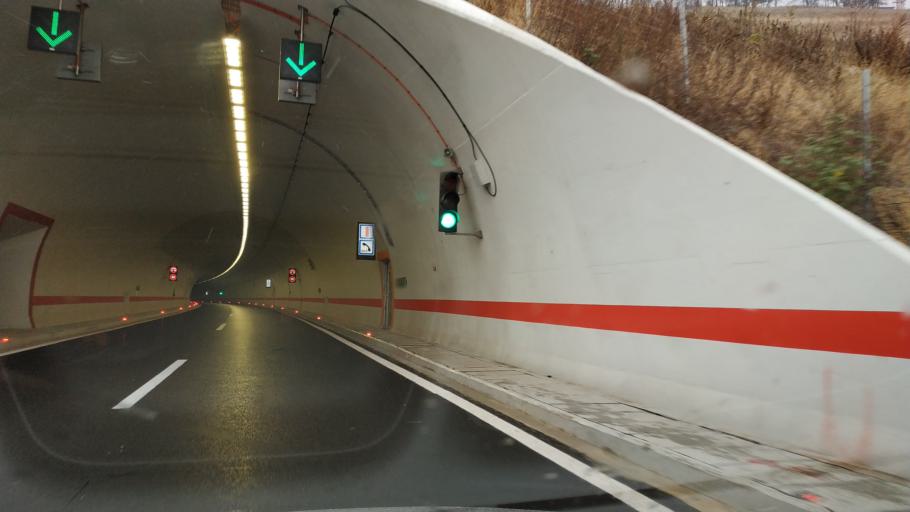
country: RS
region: Central Serbia
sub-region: Pirotski Okrug
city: Pirot
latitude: 43.1602
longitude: 22.5751
